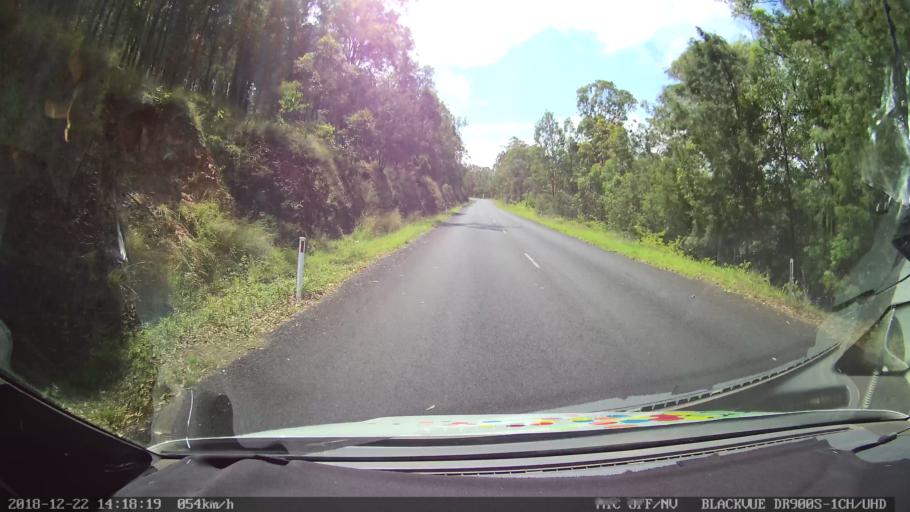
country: AU
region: New South Wales
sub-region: Clarence Valley
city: Coutts Crossing
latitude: -30.0084
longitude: 152.6649
